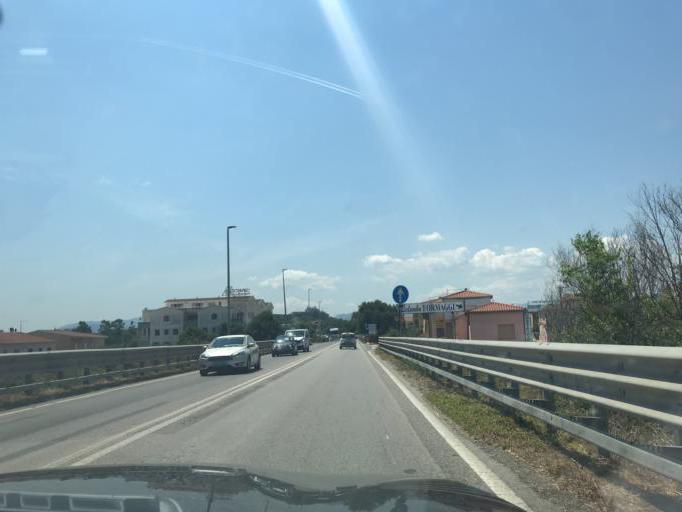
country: IT
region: Sardinia
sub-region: Provincia di Olbia-Tempio
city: Olbia
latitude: 40.9160
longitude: 9.5016
